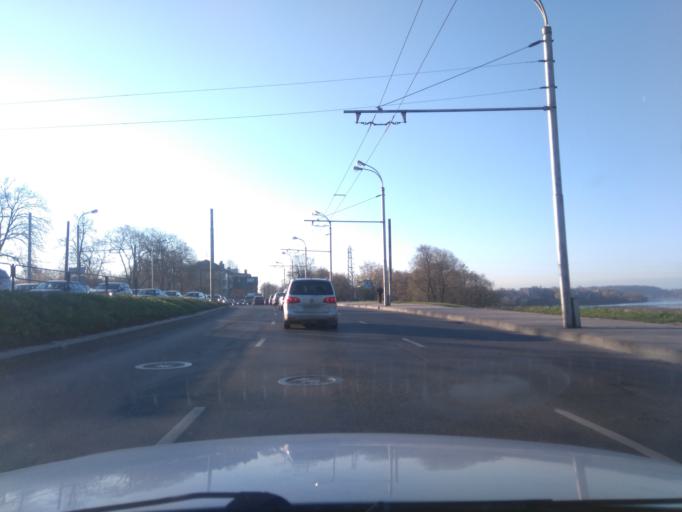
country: LT
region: Kauno apskritis
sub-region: Kaunas
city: Aleksotas
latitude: 54.8825
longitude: 23.9268
